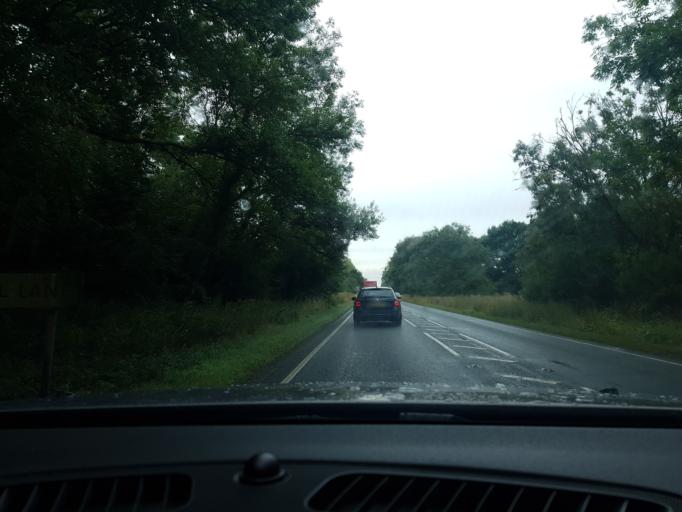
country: GB
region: England
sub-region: Hampshire
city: Fleet
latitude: 51.2458
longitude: -0.8638
